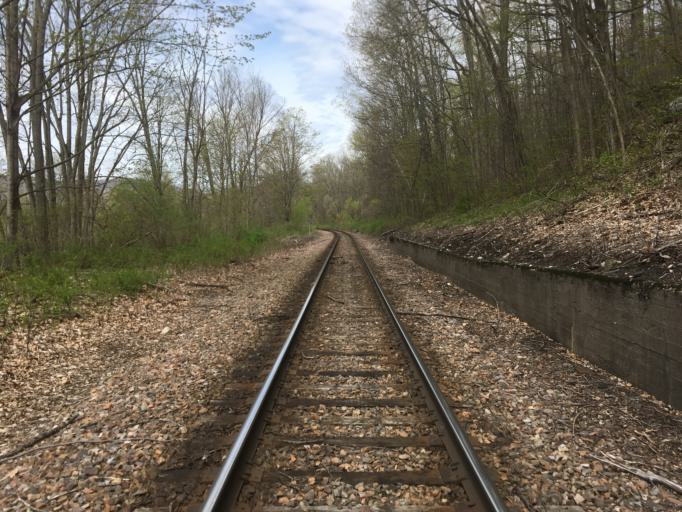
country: US
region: Vermont
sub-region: Rutland County
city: Brandon
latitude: 43.7128
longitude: -73.0405
